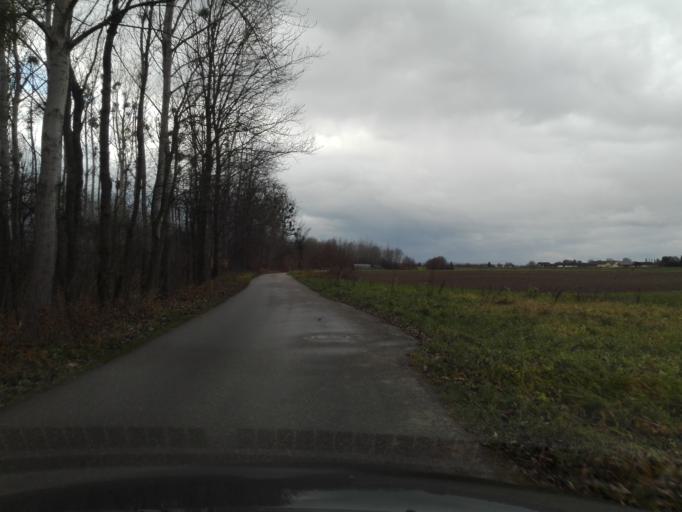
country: AT
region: Lower Austria
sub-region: Politischer Bezirk Amstetten
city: Strengberg
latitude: 48.1777
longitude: 14.7000
